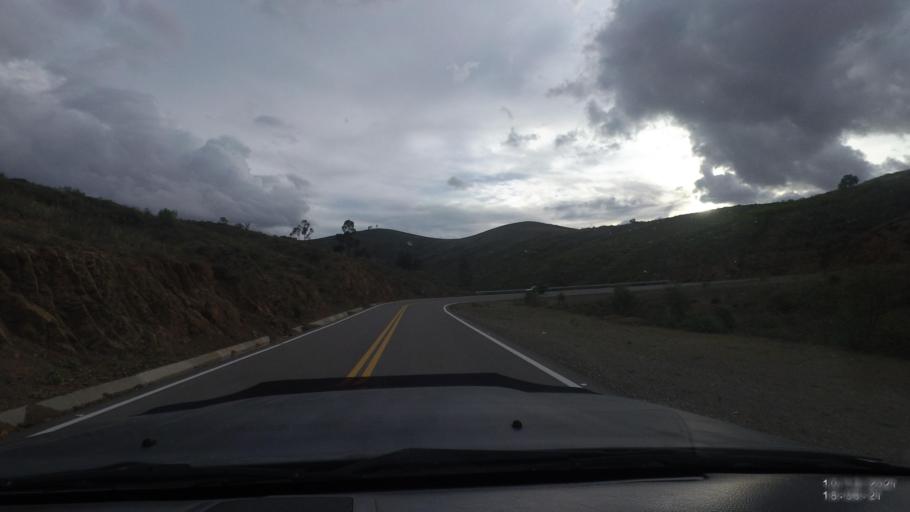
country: BO
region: Cochabamba
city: Tarata
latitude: -17.7916
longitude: -65.9454
